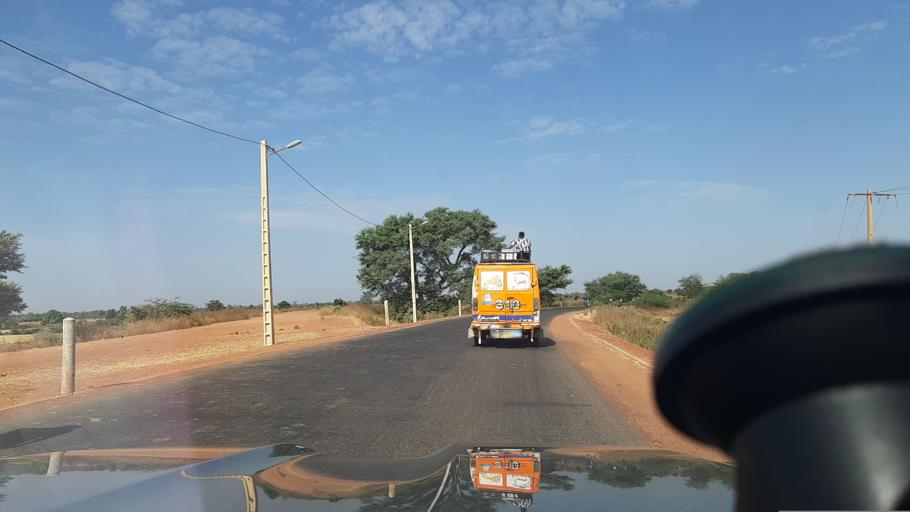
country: ML
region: Segou
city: Markala
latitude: 13.6859
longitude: -6.0982
